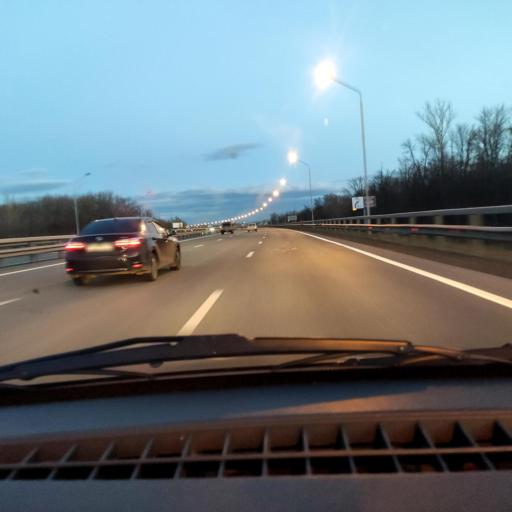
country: RU
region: Bashkortostan
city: Ufa
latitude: 54.6507
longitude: 55.9060
